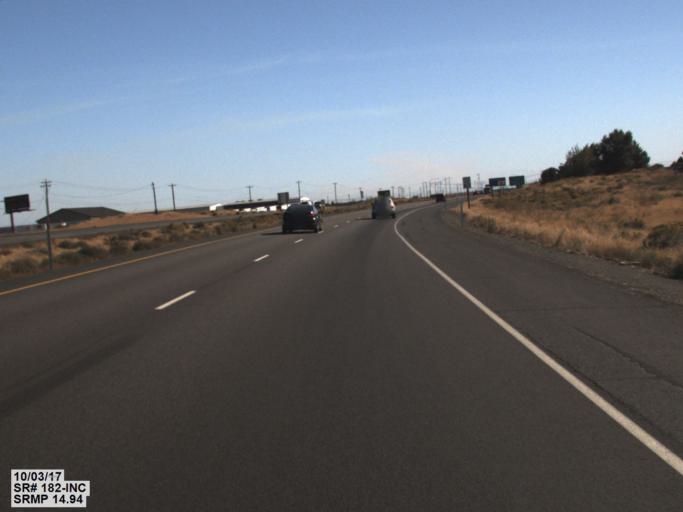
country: US
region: Washington
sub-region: Franklin County
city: Pasco
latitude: 46.2493
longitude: -119.0717
